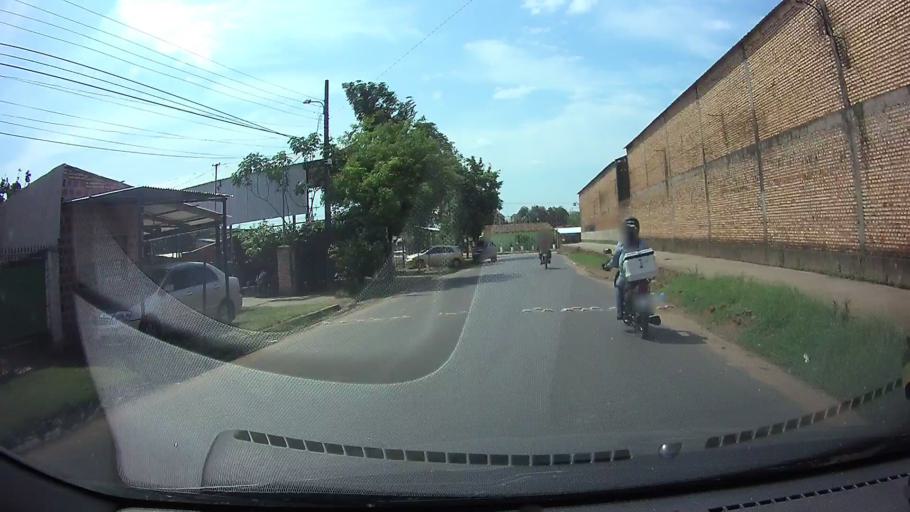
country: PY
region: Central
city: San Lorenzo
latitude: -25.3323
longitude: -57.4924
